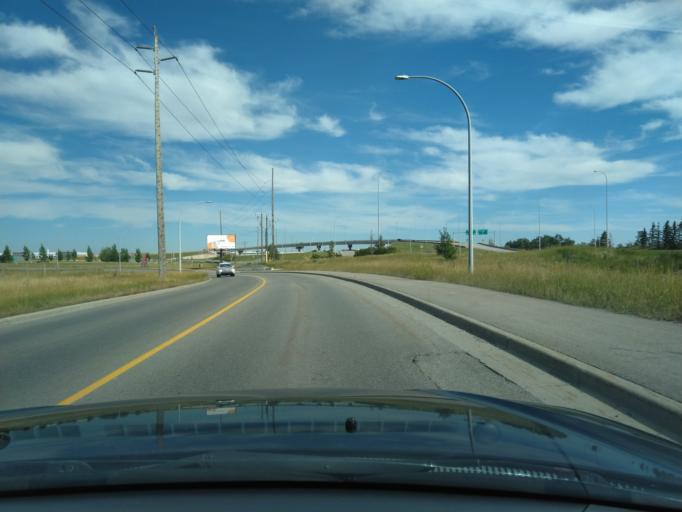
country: CA
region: Alberta
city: Calgary
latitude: 51.0960
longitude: -113.9902
